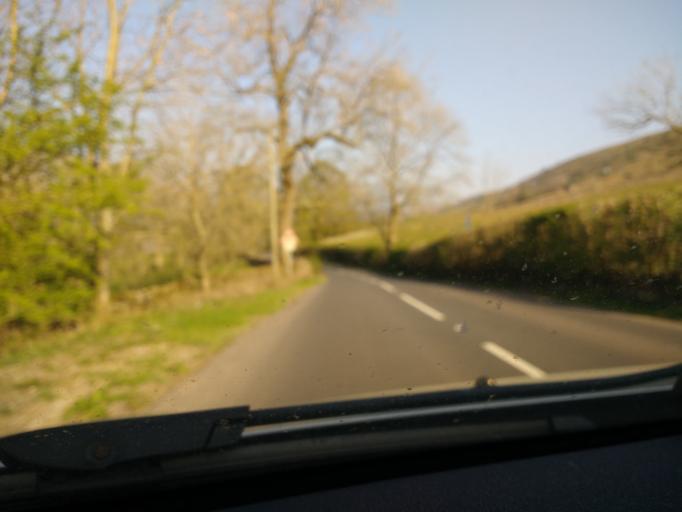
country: GB
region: England
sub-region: Cumbria
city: Sedbergh
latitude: 54.3115
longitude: -2.4525
